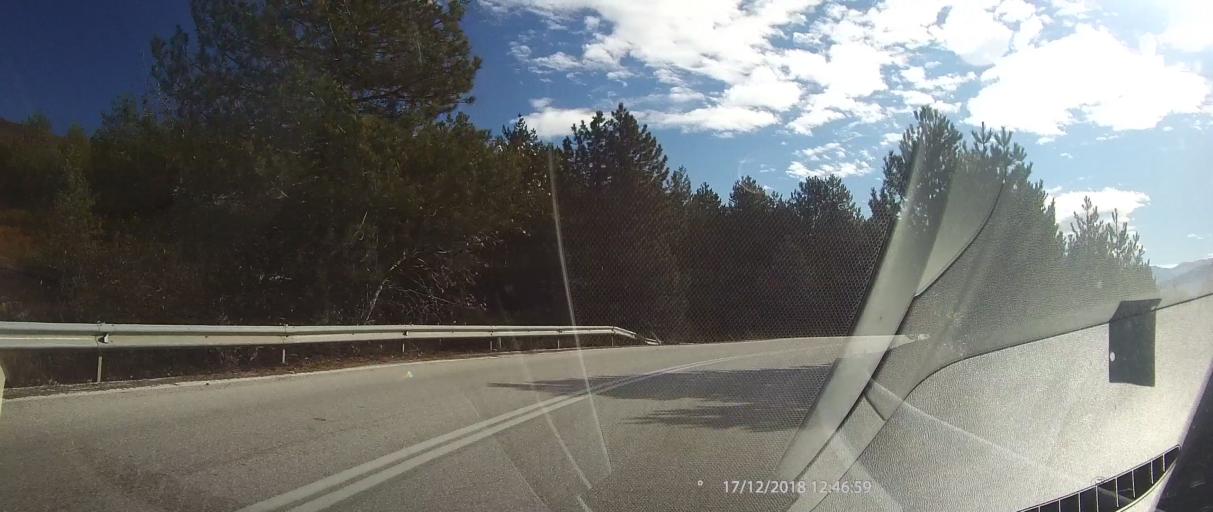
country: GR
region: Thessaly
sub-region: Trikala
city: Kastraki
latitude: 39.7871
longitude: 21.4227
